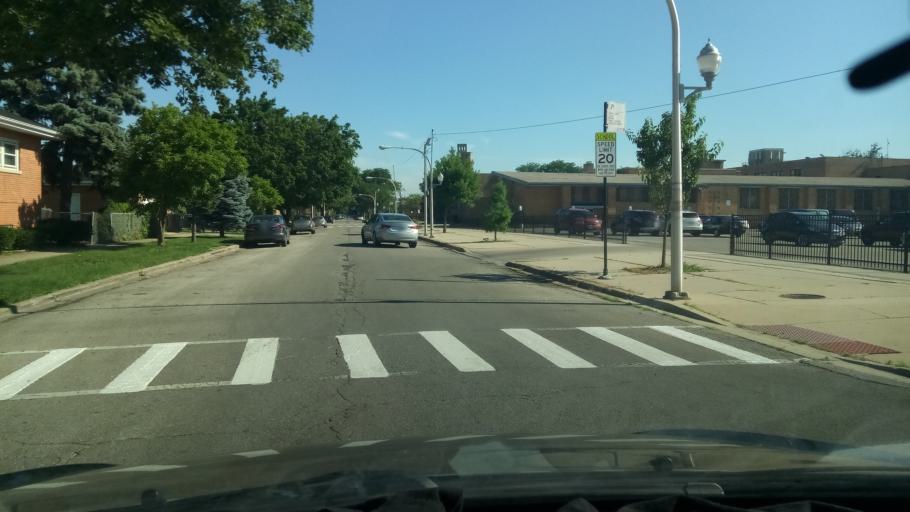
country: US
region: Illinois
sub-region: Cook County
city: Hometown
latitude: 41.7745
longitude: -87.7349
